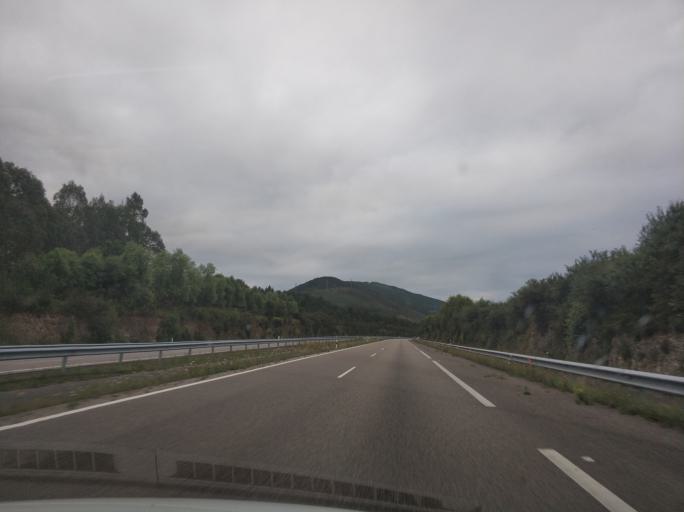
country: ES
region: Asturias
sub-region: Province of Asturias
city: Tineo
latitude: 43.5420
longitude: -6.4738
